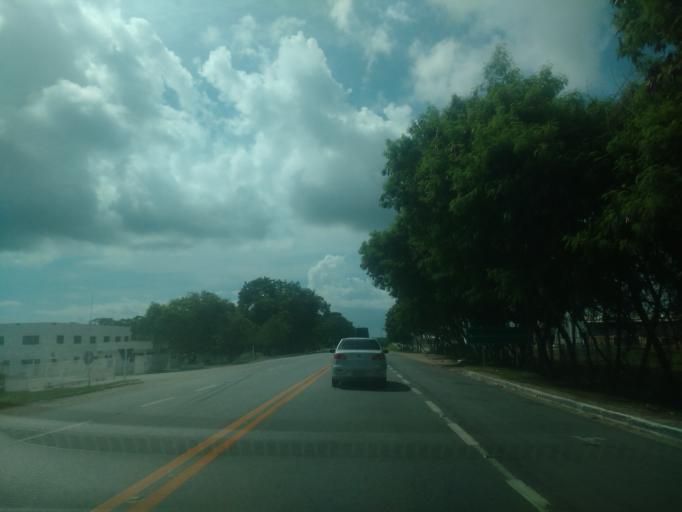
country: BR
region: Alagoas
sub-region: Marechal Deodoro
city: Marechal Deodoro
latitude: -9.6812
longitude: -35.8305
